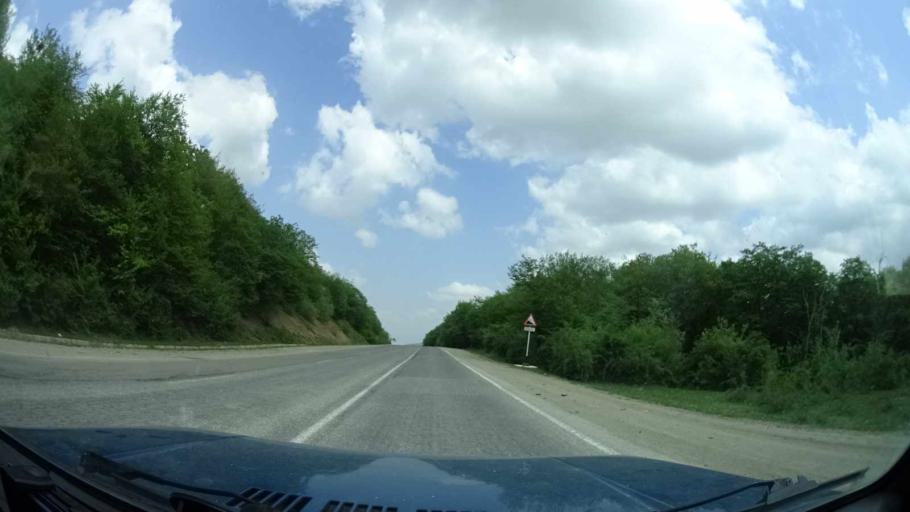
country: RU
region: Dagestan
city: Erpeli
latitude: 42.7852
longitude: 46.9767
